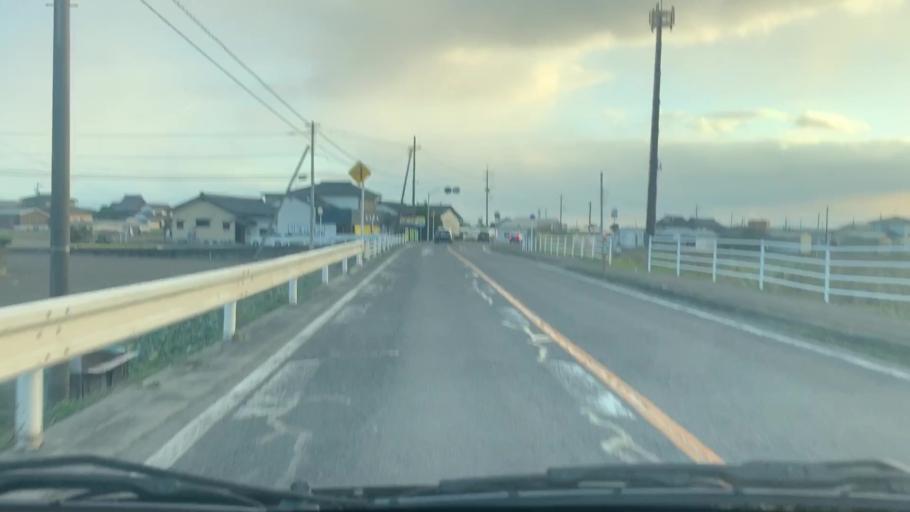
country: JP
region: Saga Prefecture
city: Saga-shi
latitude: 33.1888
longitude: 130.1931
